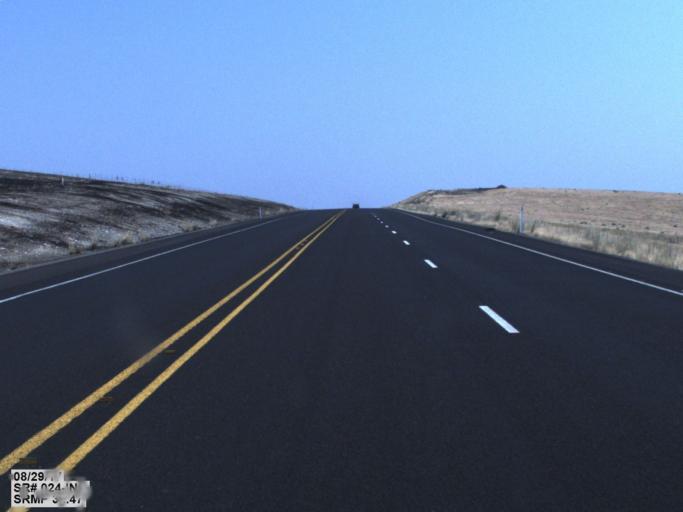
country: US
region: Washington
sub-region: Grant County
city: Desert Aire
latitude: 46.5444
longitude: -119.8413
